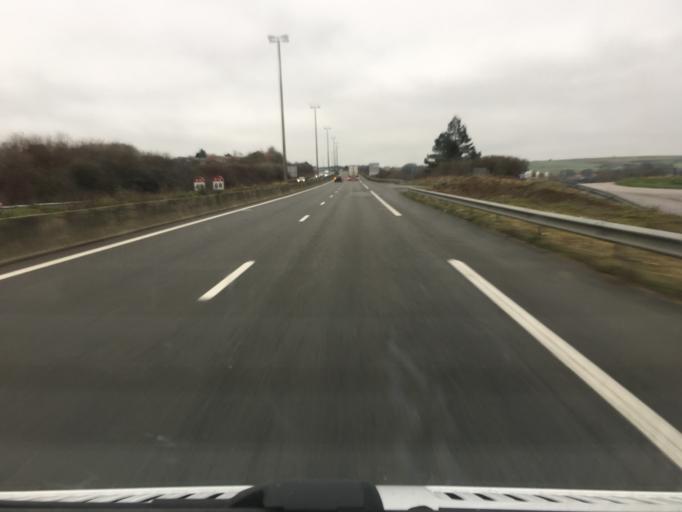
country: FR
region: Nord-Pas-de-Calais
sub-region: Departement du Pas-de-Calais
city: Marquise
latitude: 50.8499
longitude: 1.7233
